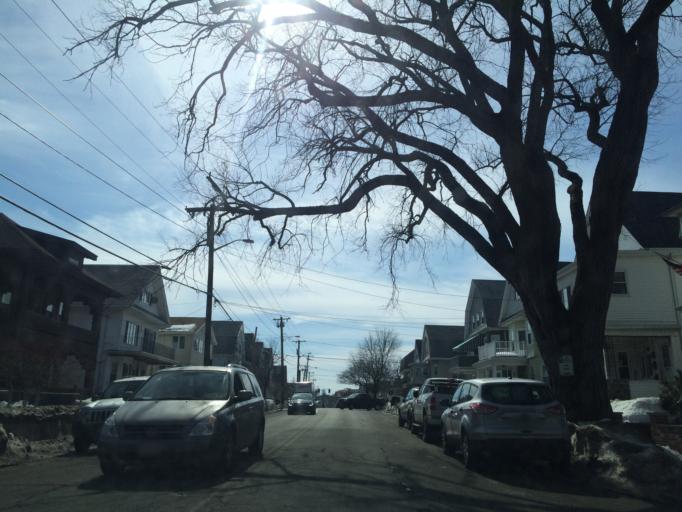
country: US
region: Massachusetts
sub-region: Middlesex County
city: Medford
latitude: 42.4070
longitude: -71.1087
